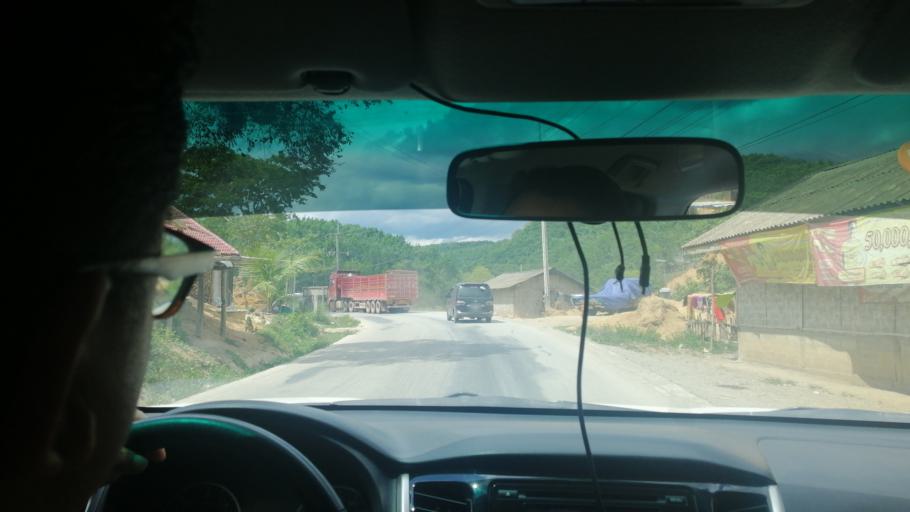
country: LA
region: Loungnamtha
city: Louang Namtha
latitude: 21.0401
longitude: 101.6503
